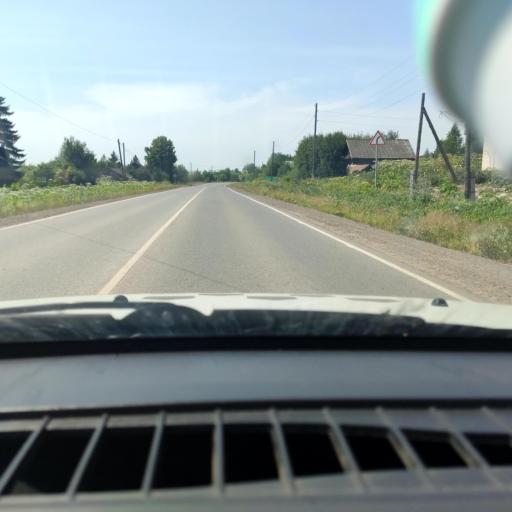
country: RU
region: Perm
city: Okhansk
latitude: 57.7047
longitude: 55.2852
